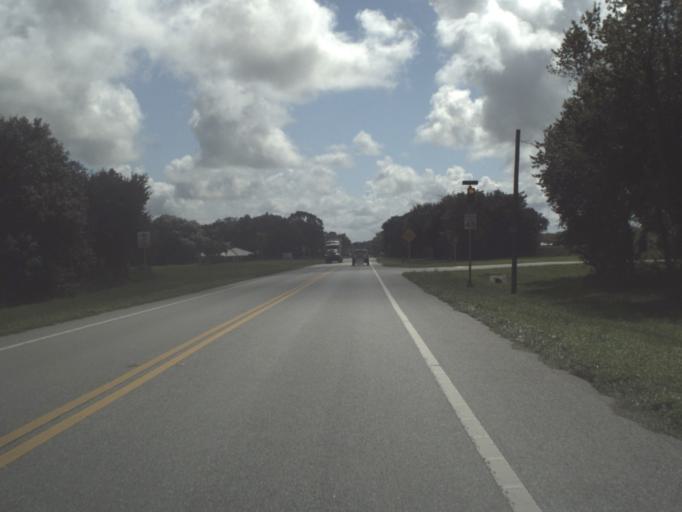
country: US
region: Florida
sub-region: Sarasota County
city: Lake Sarasota
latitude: 27.3510
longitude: -82.1667
